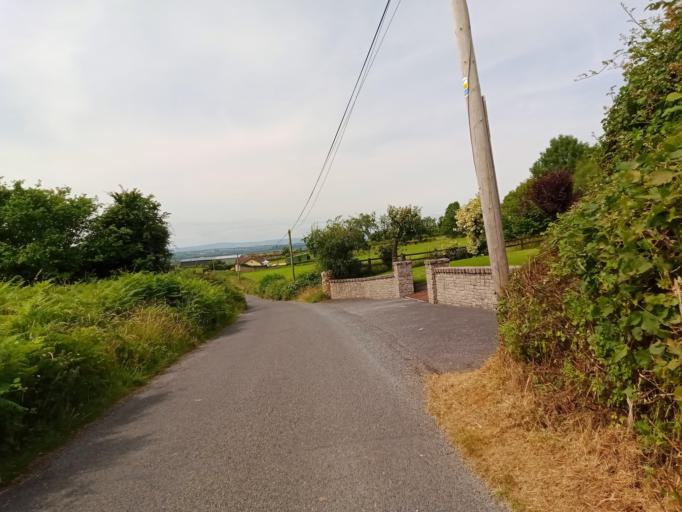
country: IE
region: Leinster
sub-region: Laois
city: Rathdowney
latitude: 52.8030
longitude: -7.4613
